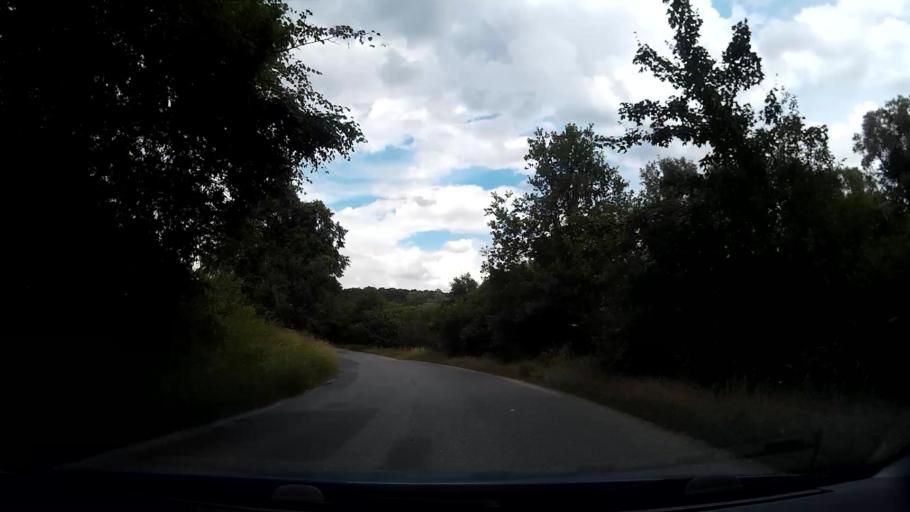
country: CZ
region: South Moravian
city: Ostopovice
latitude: 49.1421
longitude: 16.5317
